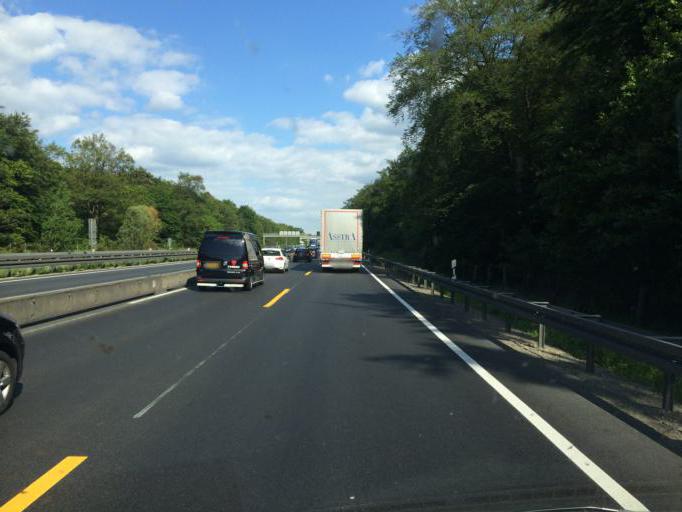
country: DE
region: Lower Saxony
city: Lehrte
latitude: 52.3958
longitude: 9.9105
